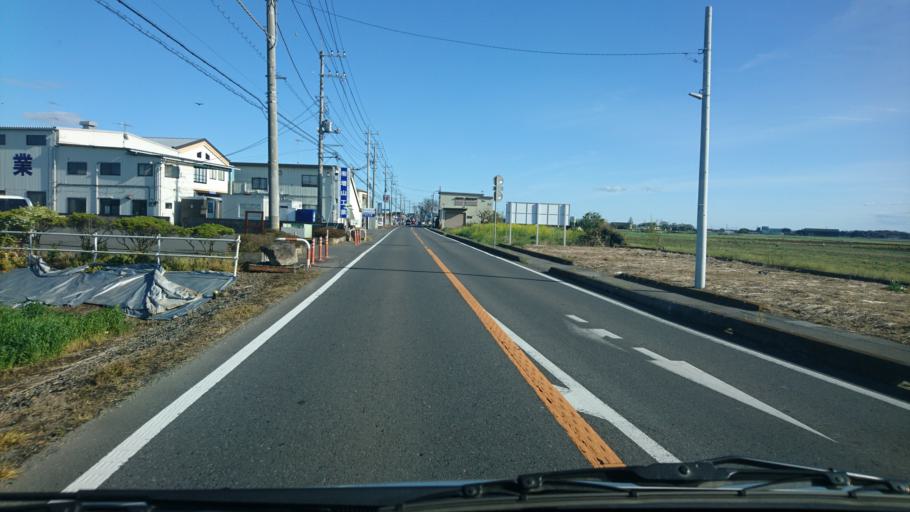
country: JP
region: Ibaraki
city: Yuki
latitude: 36.2909
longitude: 139.8937
